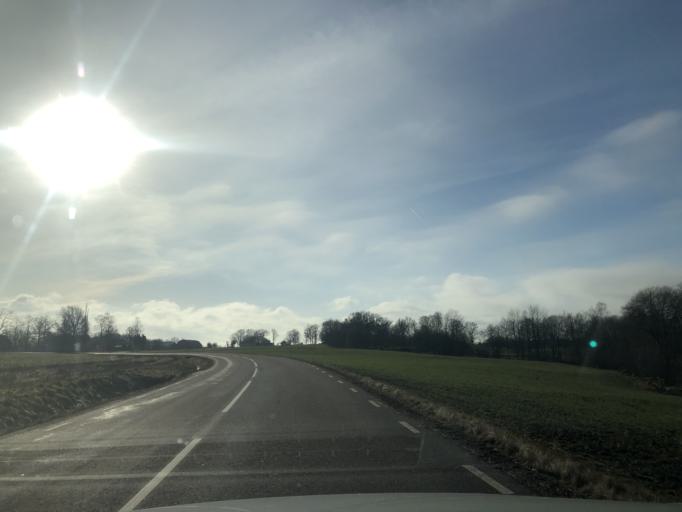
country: SE
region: Vaestra Goetaland
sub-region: Ulricehamns Kommun
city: Ulricehamn
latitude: 57.6693
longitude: 13.4011
